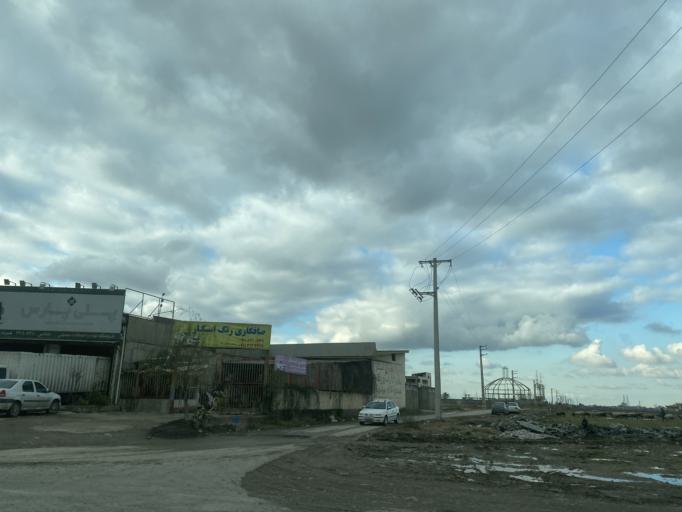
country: IR
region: Mazandaran
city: Amol
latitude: 36.4369
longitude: 52.3735
